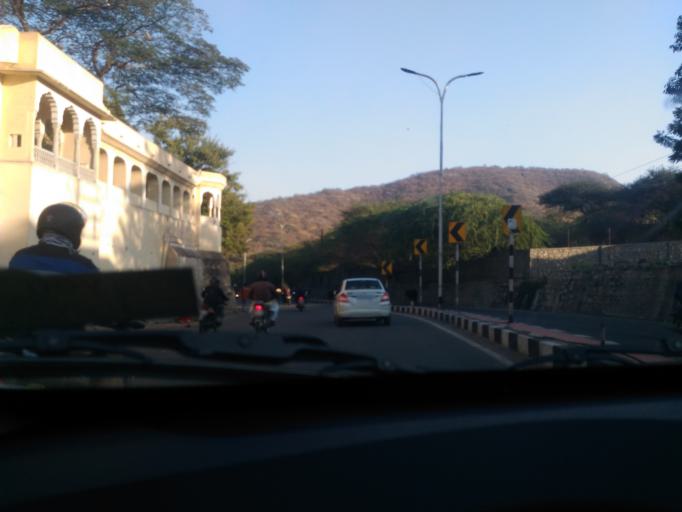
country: IN
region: Rajasthan
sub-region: Jaipur
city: Jaipur
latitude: 26.9020
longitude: 75.8467
